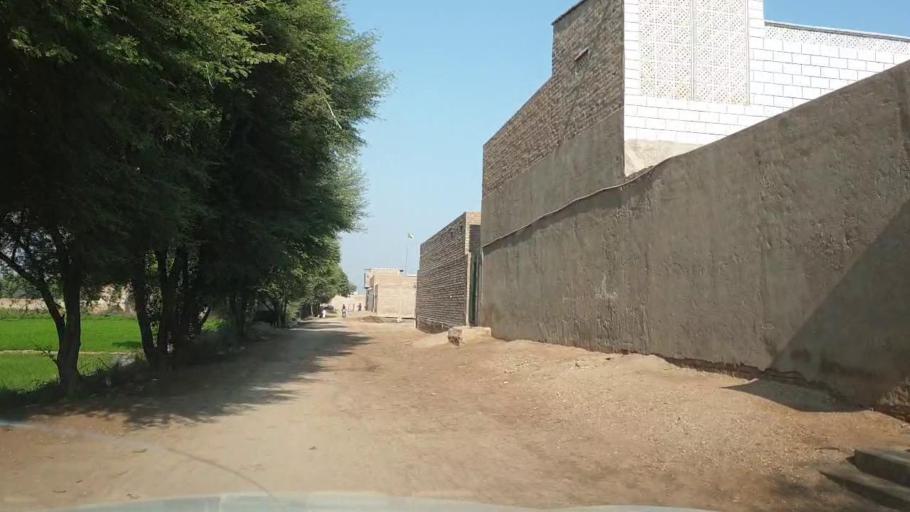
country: PK
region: Sindh
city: Bhan
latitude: 26.5461
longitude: 67.7438
